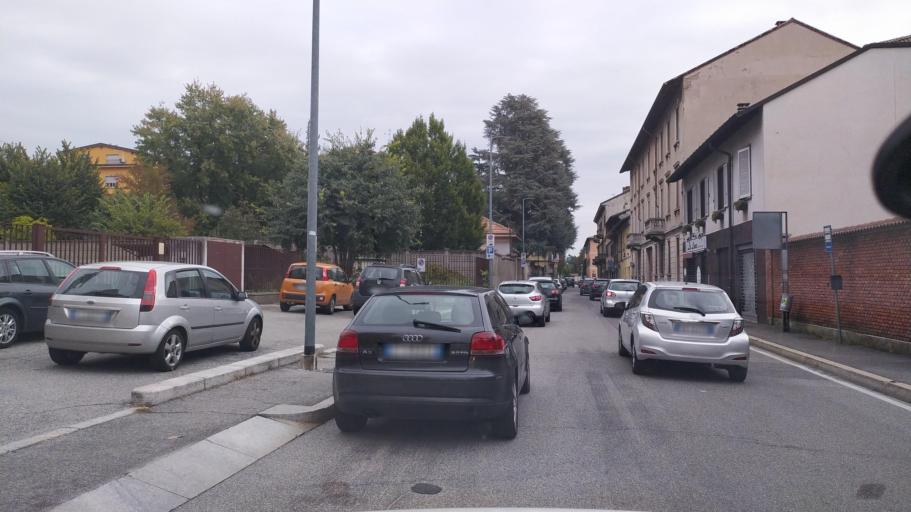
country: IT
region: Lombardy
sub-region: Provincia di Monza e Brianza
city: Seregno
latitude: 45.6469
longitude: 9.2088
